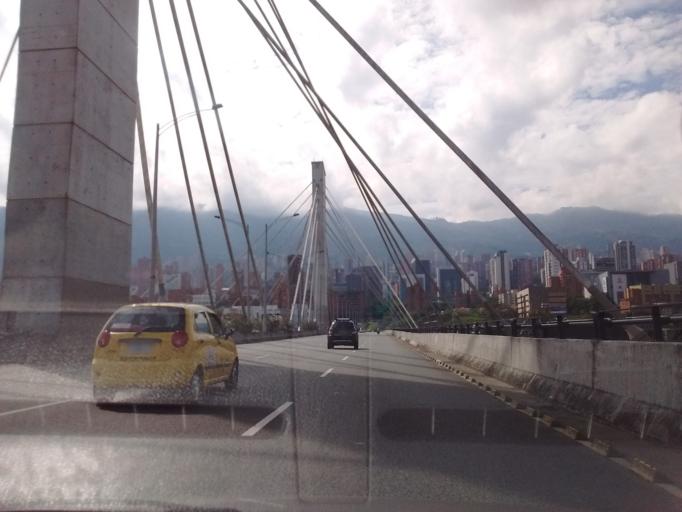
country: CO
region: Antioquia
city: Itagui
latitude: 6.2041
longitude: -75.5799
